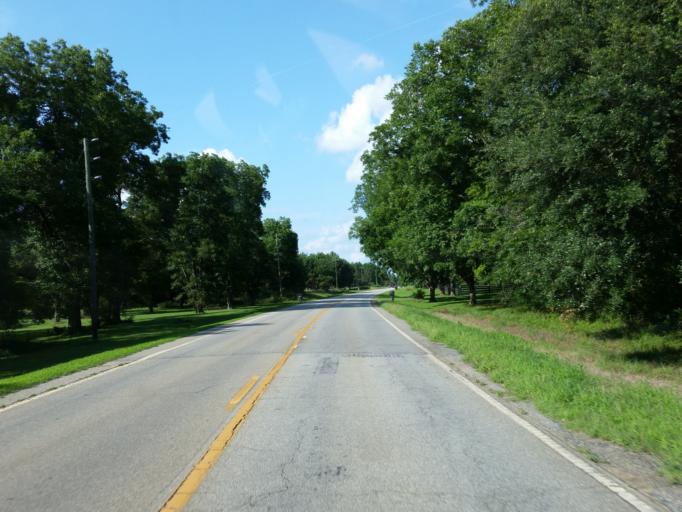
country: US
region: Georgia
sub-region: Lee County
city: Leesburg
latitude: 31.8411
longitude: -84.0943
